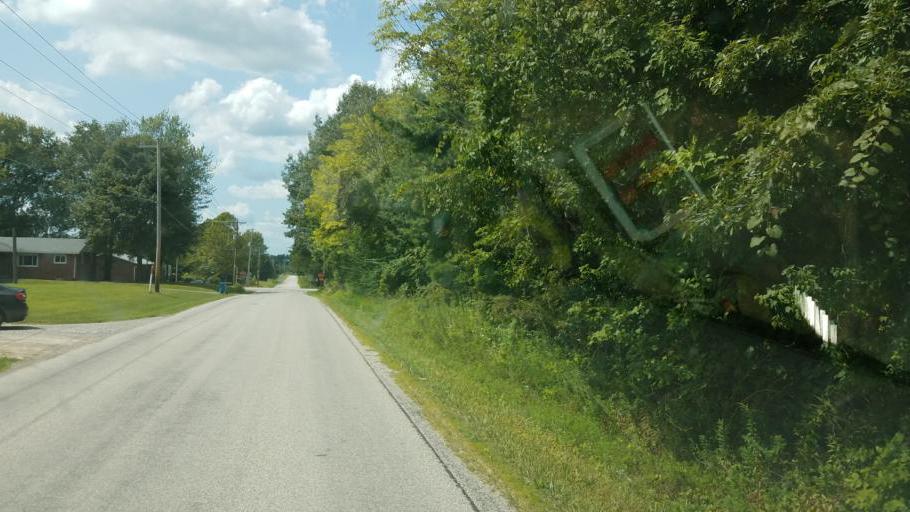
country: US
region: Ohio
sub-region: Delaware County
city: Sunbury
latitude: 40.3582
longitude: -82.8295
